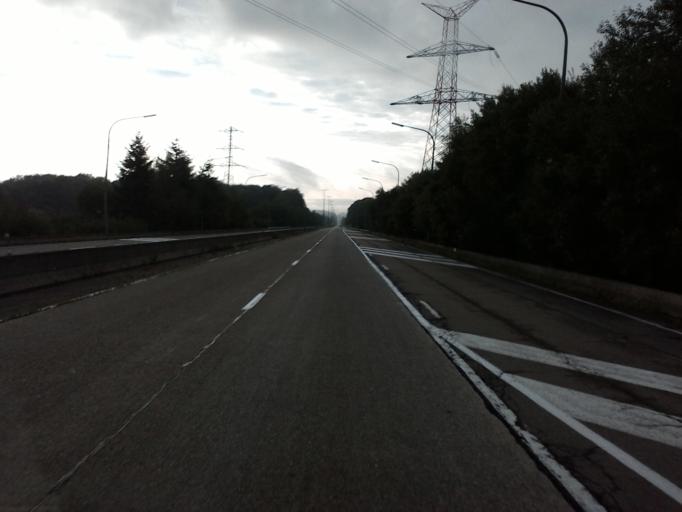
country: BE
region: Wallonia
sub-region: Province du Luxembourg
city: Attert
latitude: 49.7794
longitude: 5.7538
